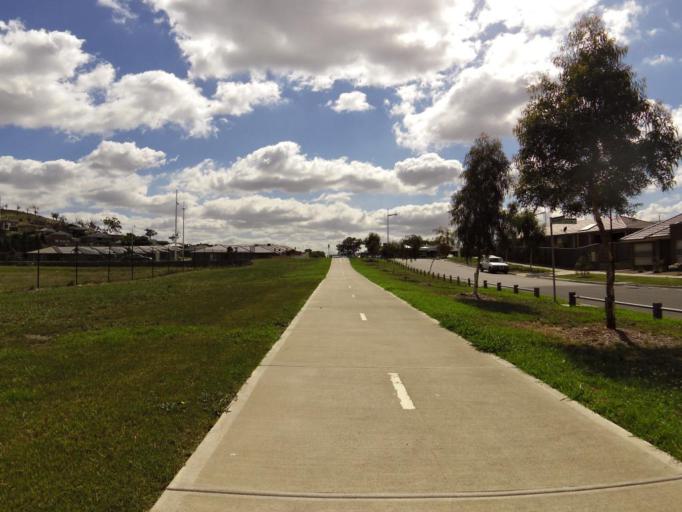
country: AU
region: Victoria
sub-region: Whittlesea
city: Mernda
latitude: -37.6319
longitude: 145.0859
